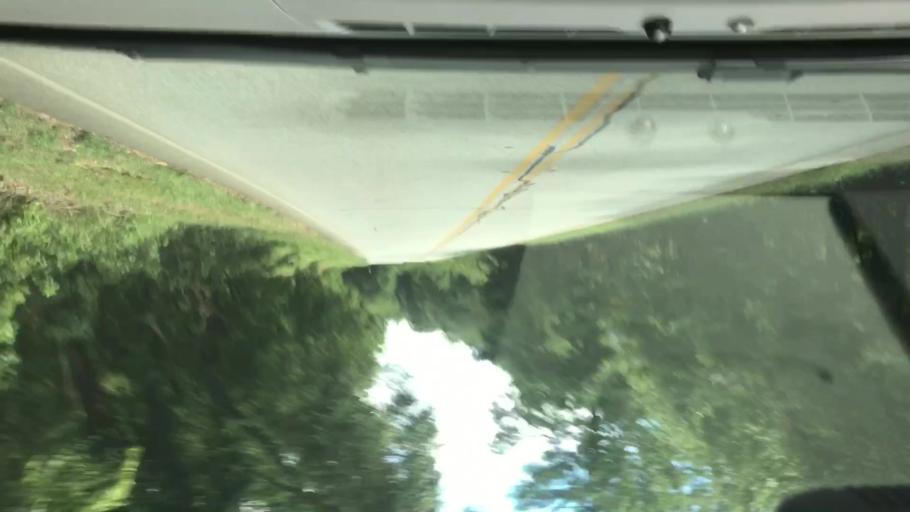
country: US
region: Georgia
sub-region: Stewart County
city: Lumpkin
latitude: 32.1387
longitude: -84.8480
